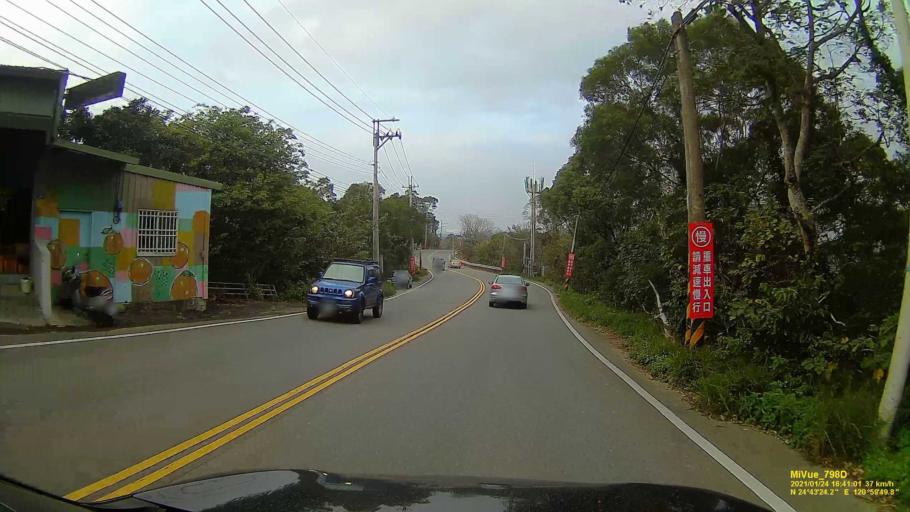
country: TW
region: Taiwan
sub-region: Hsinchu
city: Hsinchu
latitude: 24.7234
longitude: 120.9977
